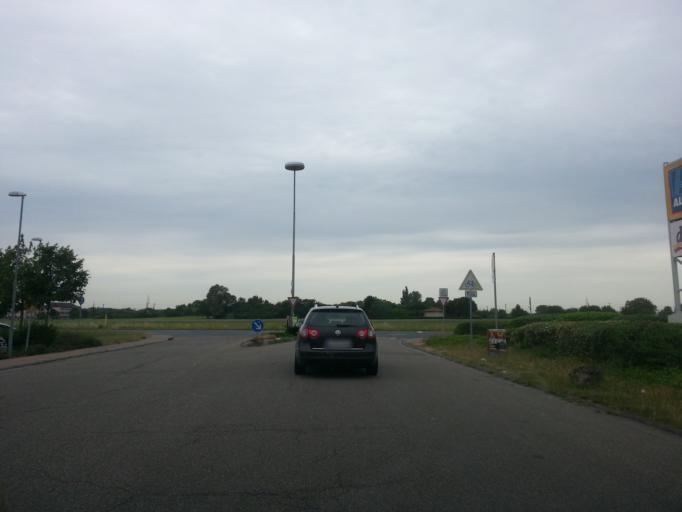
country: DE
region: Baden-Wuerttemberg
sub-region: Karlsruhe Region
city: Edingen-Neckarhausen
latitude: 49.4558
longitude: 8.5952
